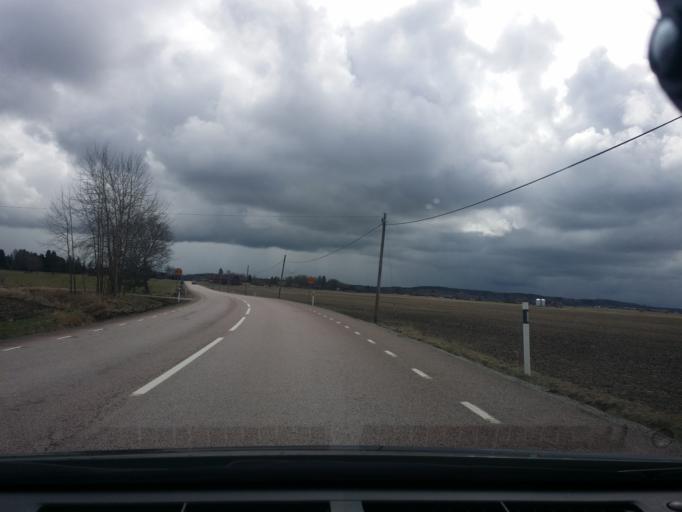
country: SE
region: Uppsala
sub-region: Enkopings Kommun
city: Irsta
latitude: 59.7825
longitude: 16.8423
